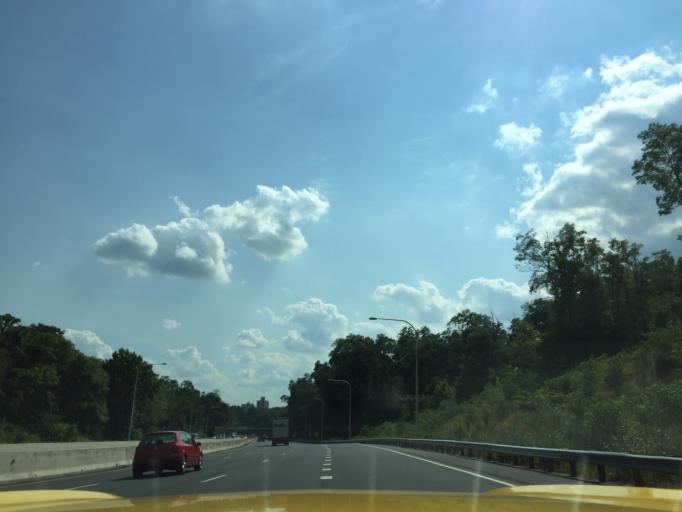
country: US
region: Delaware
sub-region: New Castle County
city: Wilmington
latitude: 39.7660
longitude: -75.5458
